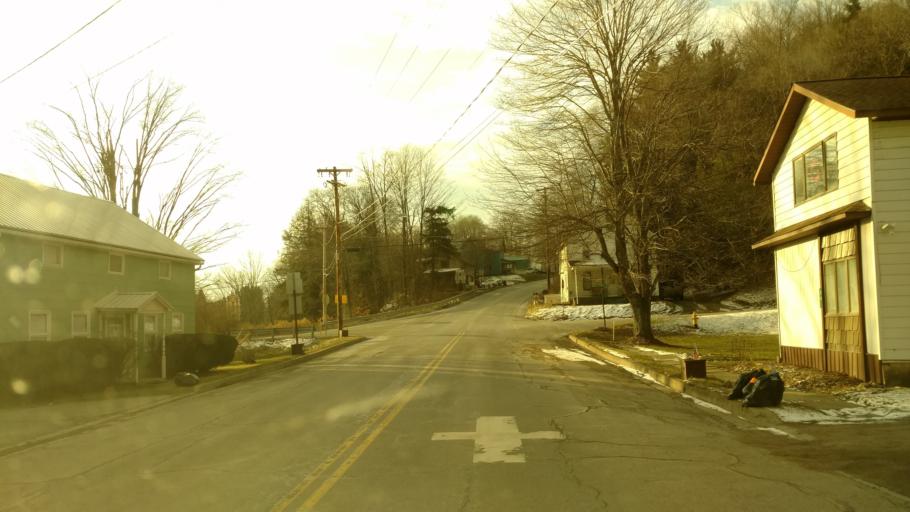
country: US
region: New York
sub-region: Allegany County
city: Wellsville
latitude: 41.9892
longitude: -77.8689
